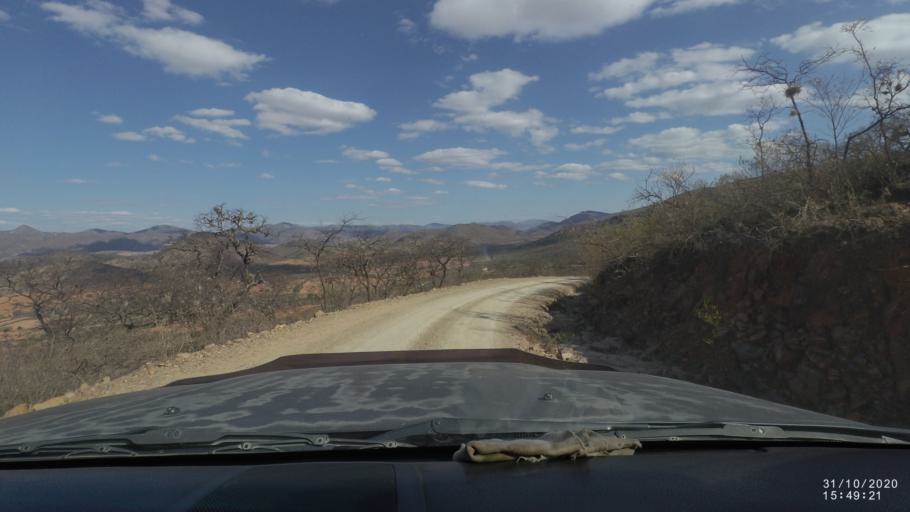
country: BO
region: Chuquisaca
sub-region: Provincia Zudanez
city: Mojocoya
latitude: -18.3107
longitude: -64.7079
